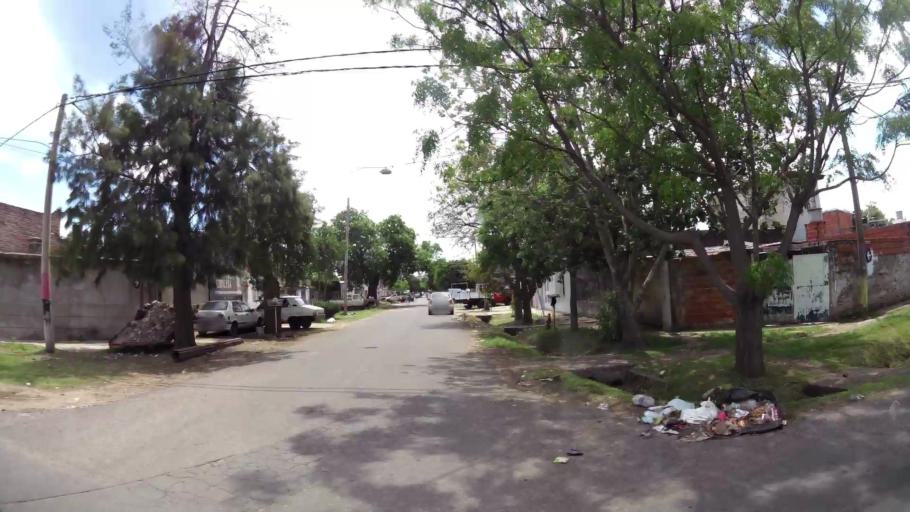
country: AR
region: Santa Fe
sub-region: Departamento de Rosario
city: Rosario
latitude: -32.9878
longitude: -60.6312
